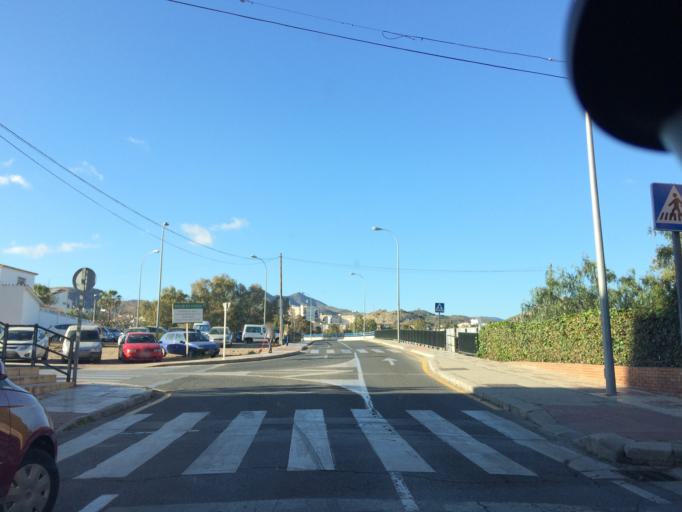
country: ES
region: Andalusia
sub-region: Provincia de Malaga
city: Malaga
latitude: 36.7261
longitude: -4.4489
